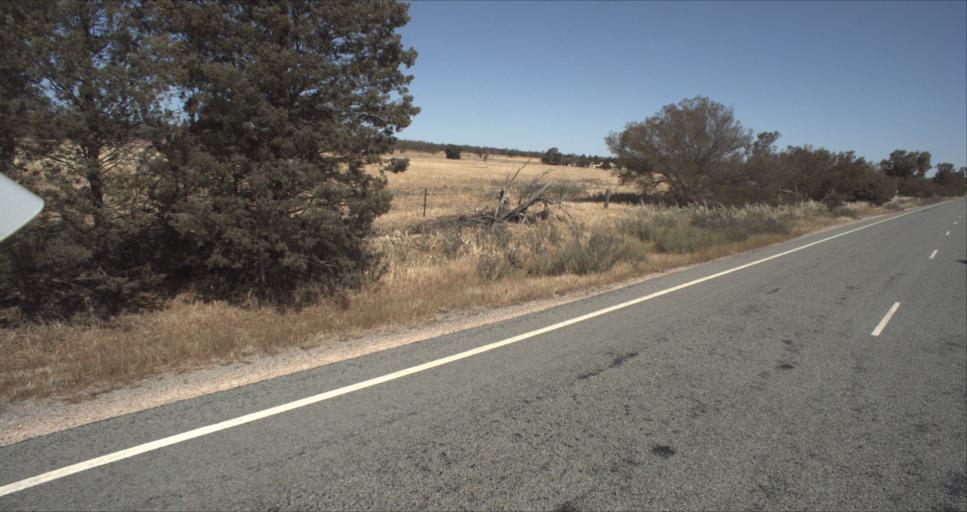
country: AU
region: New South Wales
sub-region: Leeton
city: Leeton
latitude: -34.4637
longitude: 146.4372
